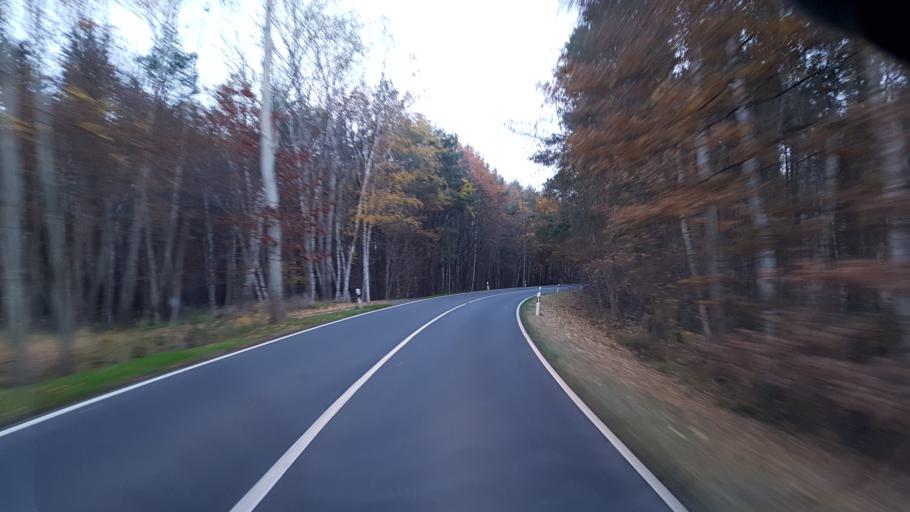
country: DE
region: Brandenburg
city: Schraden
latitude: 51.4422
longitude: 13.7072
